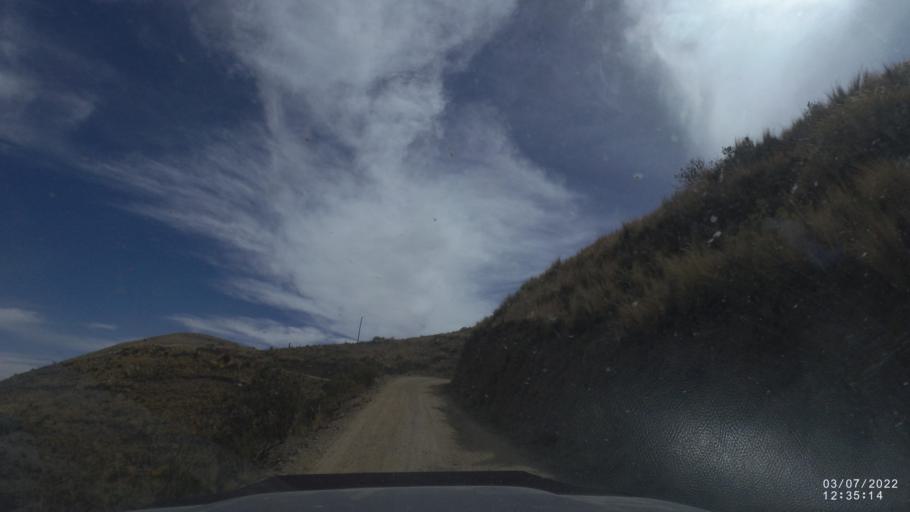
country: BO
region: Cochabamba
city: Irpa Irpa
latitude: -17.8056
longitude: -66.6076
